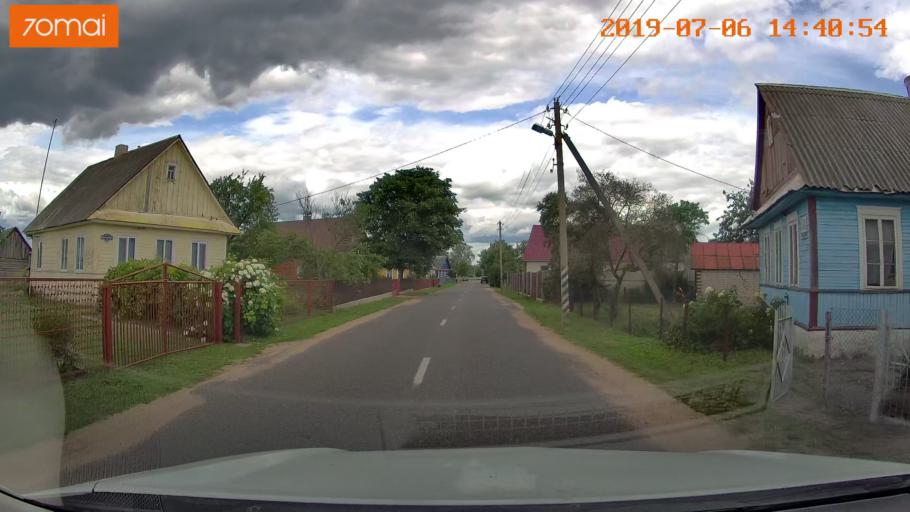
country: BY
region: Minsk
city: Ivyanyets
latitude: 53.9275
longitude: 26.6740
